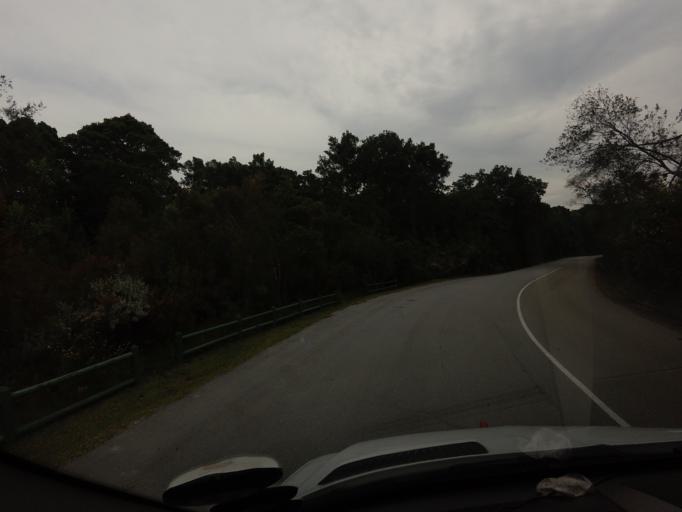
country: ZA
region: Eastern Cape
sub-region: Cacadu District Municipality
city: Kareedouw
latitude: -34.0138
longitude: 23.8722
